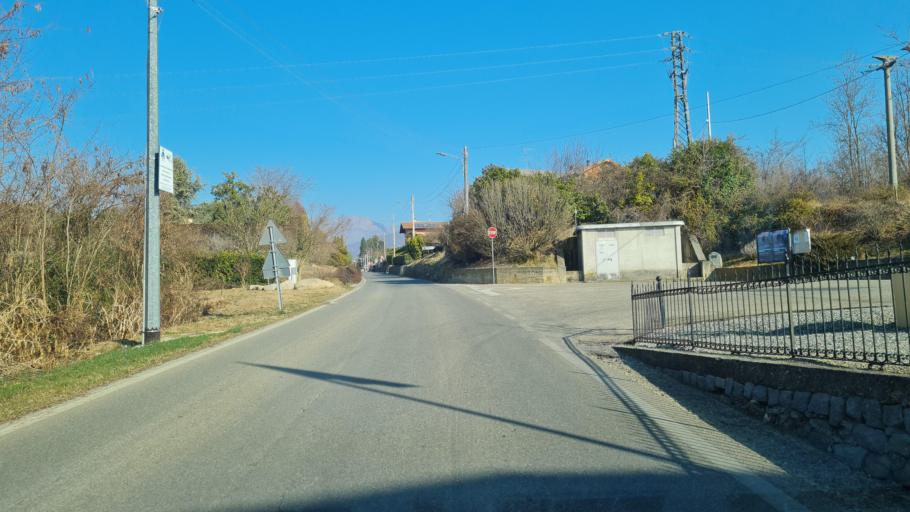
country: IT
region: Piedmont
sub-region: Provincia di Biella
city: Piatto
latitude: 45.5853
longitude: 8.1365
